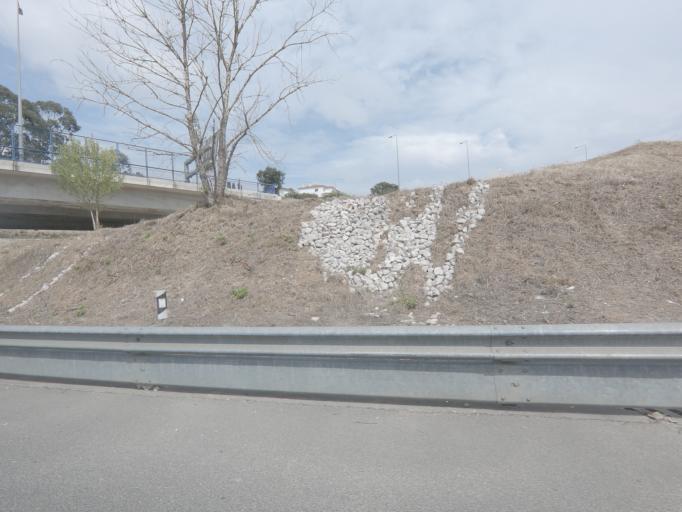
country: PT
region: Leiria
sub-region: Leiria
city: Leiria
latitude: 39.7457
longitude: -8.8188
